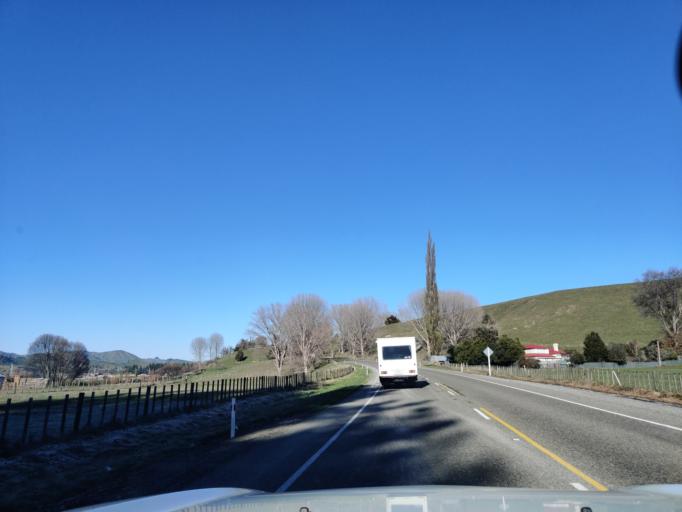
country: NZ
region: Manawatu-Wanganui
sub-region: Ruapehu District
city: Waiouru
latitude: -39.7360
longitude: 175.8418
